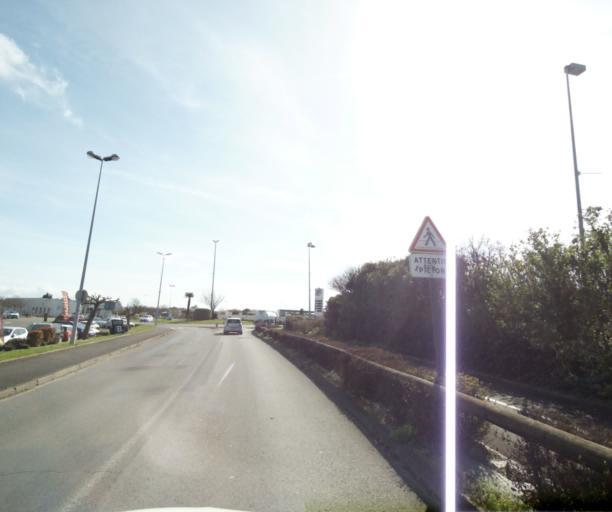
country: FR
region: Poitou-Charentes
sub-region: Departement de la Charente-Maritime
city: La Rochelle
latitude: 46.1747
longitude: -1.1669
